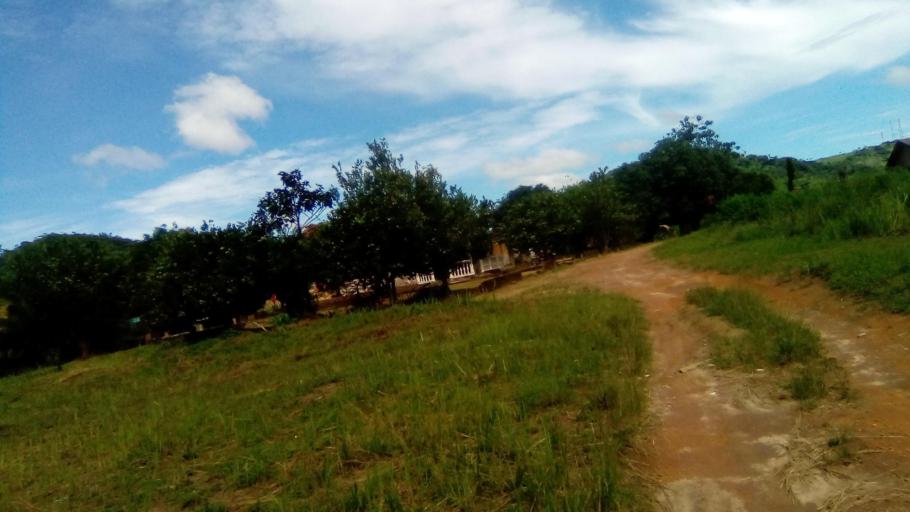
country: SL
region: Eastern Province
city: Simbakoro
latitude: 8.6365
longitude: -10.9976
